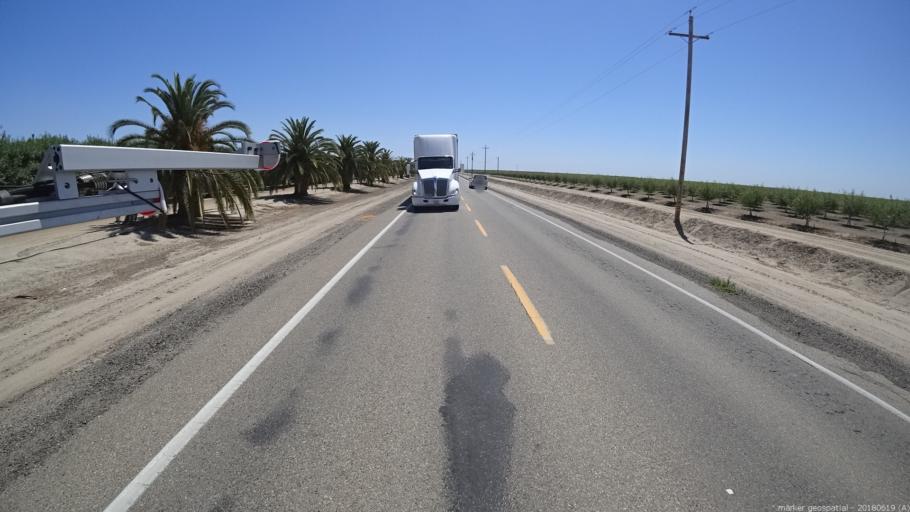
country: US
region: California
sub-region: Fresno County
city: Mendota
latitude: 36.8511
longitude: -120.2891
